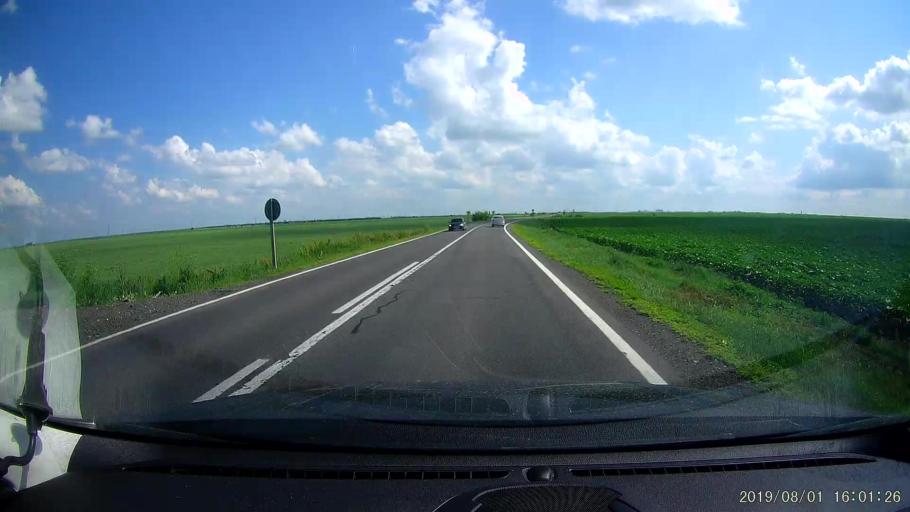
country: RO
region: Ialomita
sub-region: Comuna Ciulnita
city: Ciulnita
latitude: 44.5083
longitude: 27.3903
